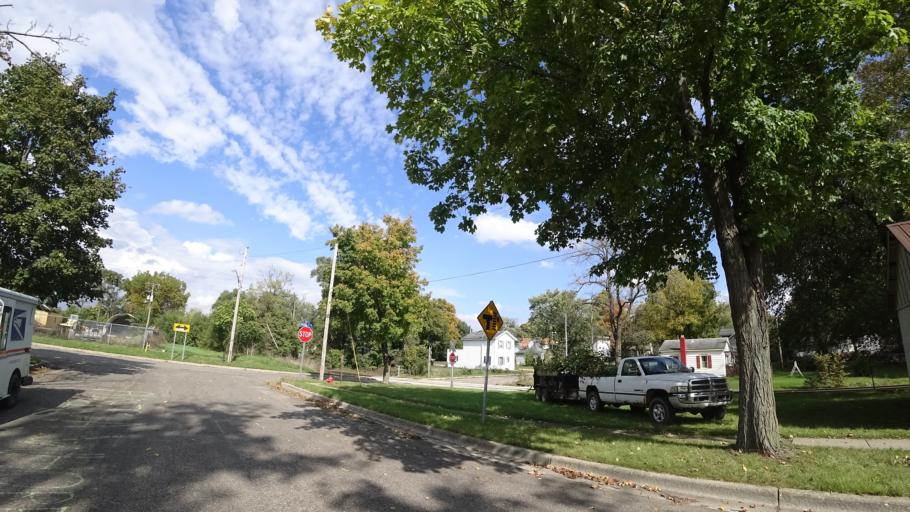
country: US
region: Michigan
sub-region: Saint Joseph County
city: Three Rivers
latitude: 41.9349
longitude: -85.6284
